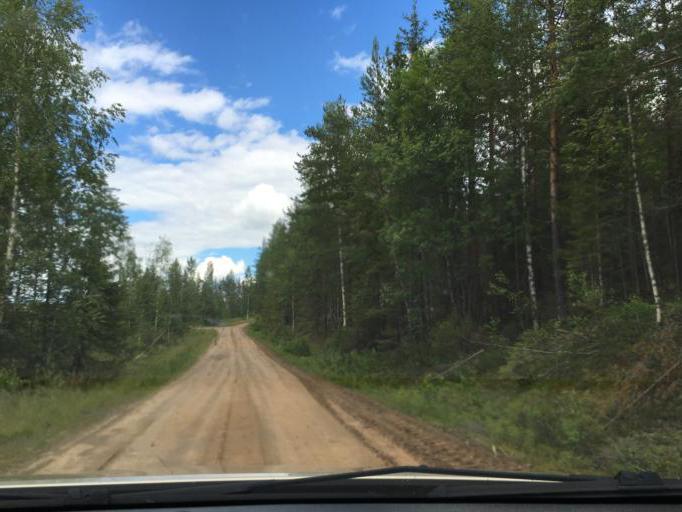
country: SE
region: Norrbotten
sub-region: Overkalix Kommun
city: OEverkalix
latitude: 66.1430
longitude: 22.7873
